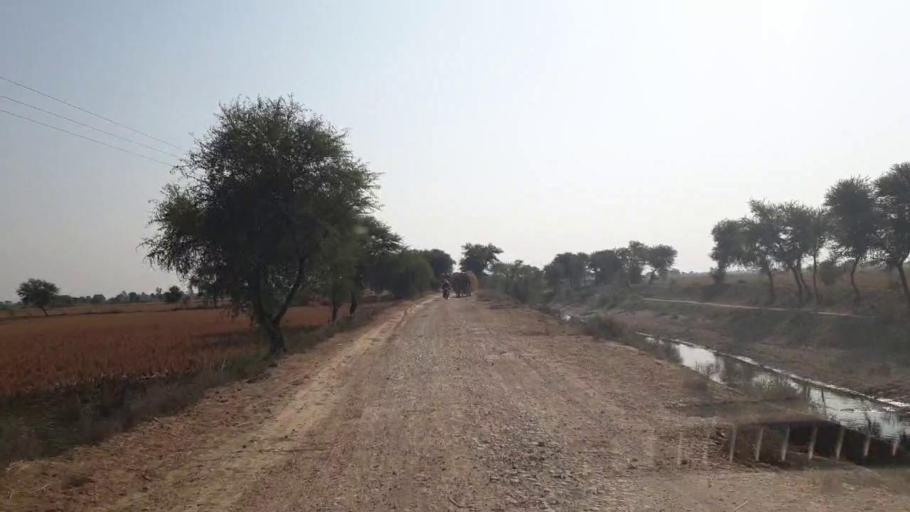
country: PK
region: Sindh
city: Kario
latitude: 24.9080
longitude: 68.6492
